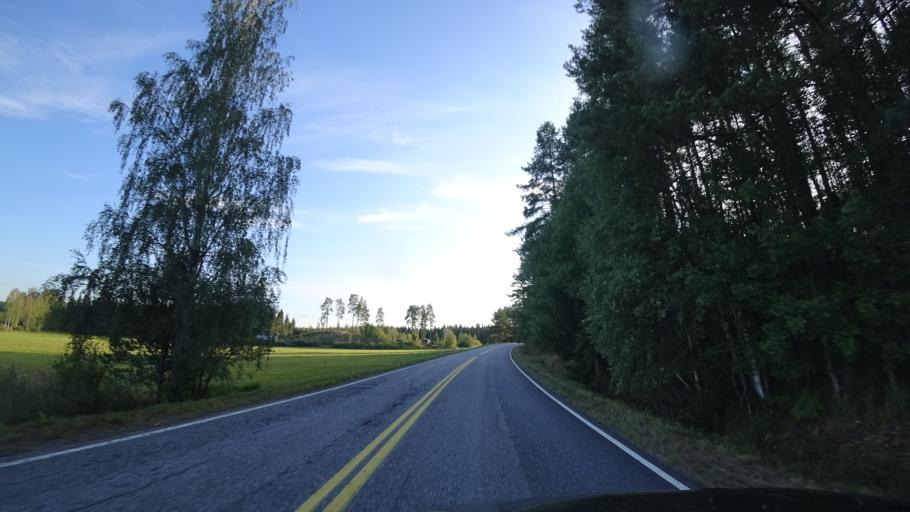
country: FI
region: Haeme
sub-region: Haemeenlinna
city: Tuulos
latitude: 61.0061
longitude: 24.8498
